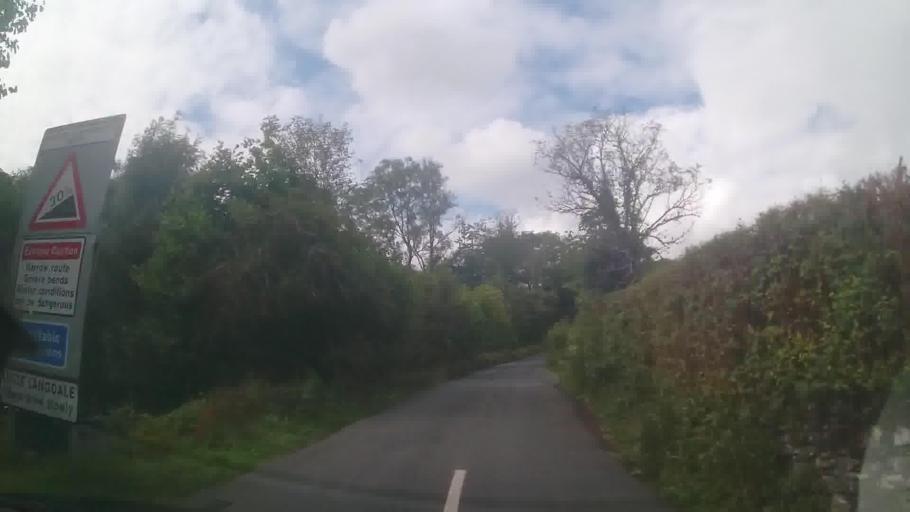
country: GB
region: England
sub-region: Cumbria
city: Ambleside
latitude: 54.4191
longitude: -3.0341
